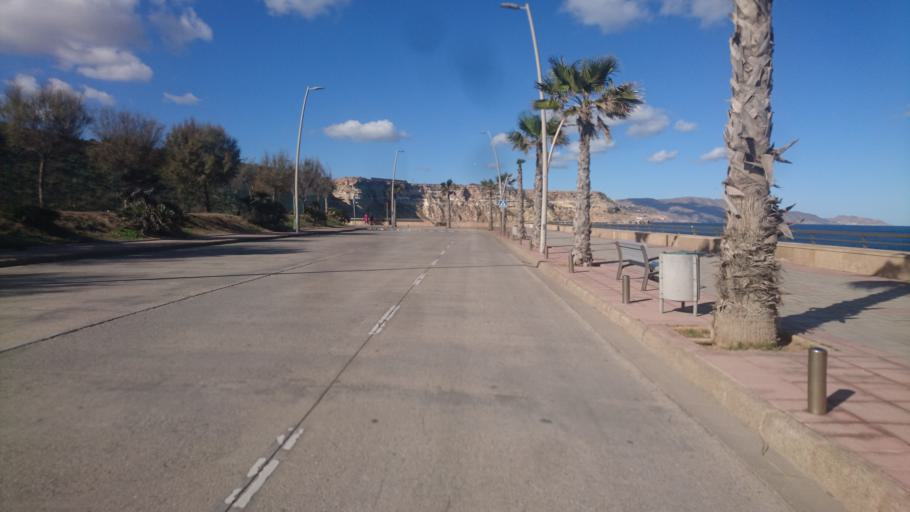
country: ES
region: Melilla
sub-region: Melilla
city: Melilla
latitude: 35.3027
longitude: -2.9386
